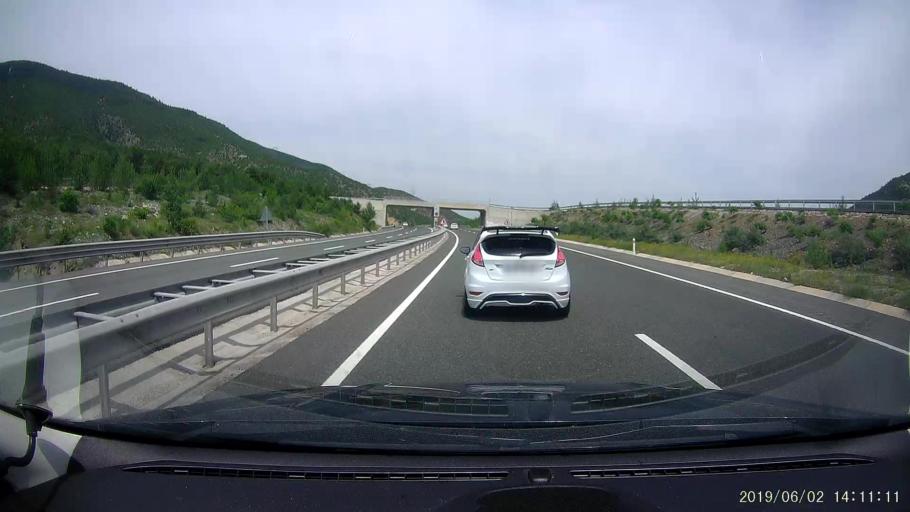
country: TR
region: Cankiri
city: Yaprakli
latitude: 40.9064
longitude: 33.7796
